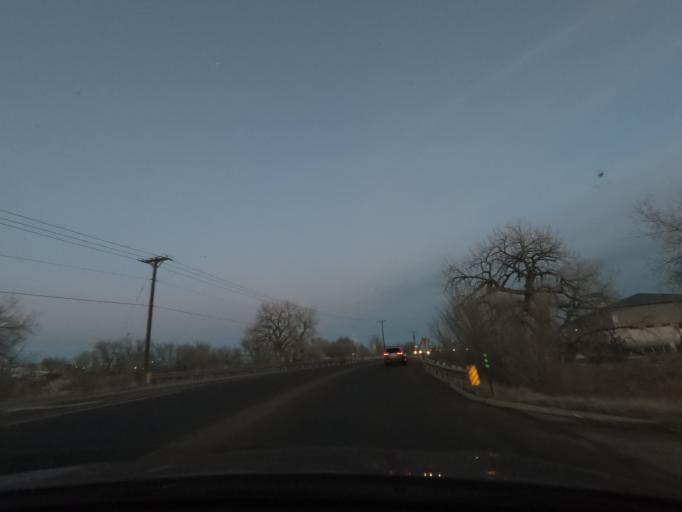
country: US
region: Colorado
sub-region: El Paso County
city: Stratmoor
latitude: 38.7776
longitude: -104.7763
